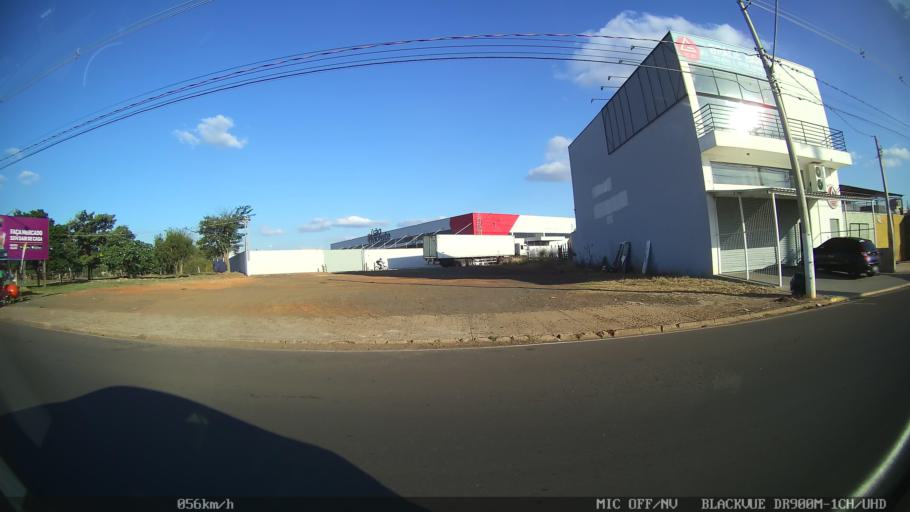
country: BR
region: Sao Paulo
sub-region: Americana
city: Americana
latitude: -22.7368
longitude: -47.3621
